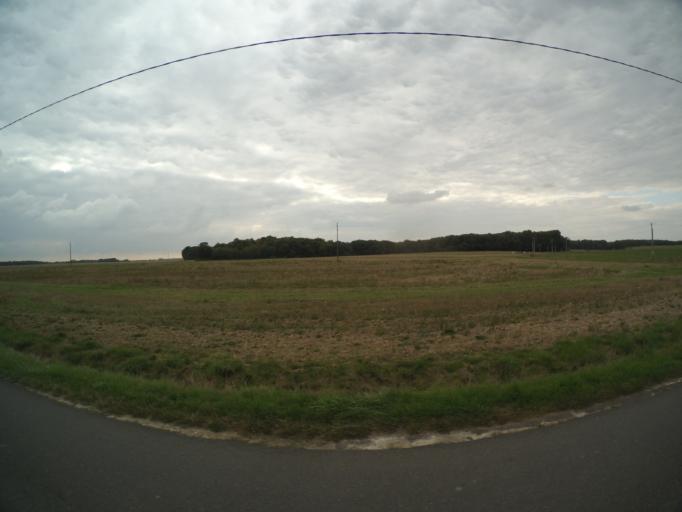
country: FR
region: Centre
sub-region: Departement d'Indre-et-Loire
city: Auzouer-en-Touraine
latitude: 47.4953
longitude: 0.9329
